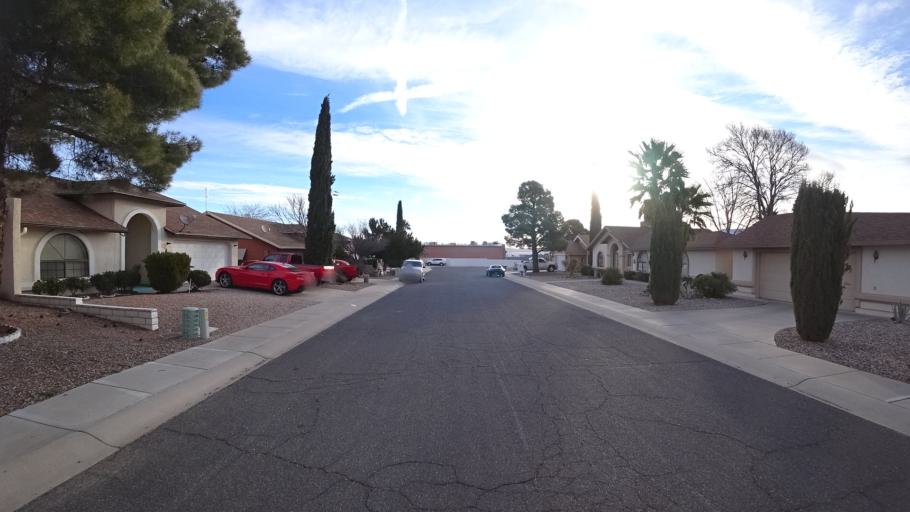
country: US
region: Arizona
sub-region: Mohave County
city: New Kingman-Butler
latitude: 35.2410
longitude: -114.0412
